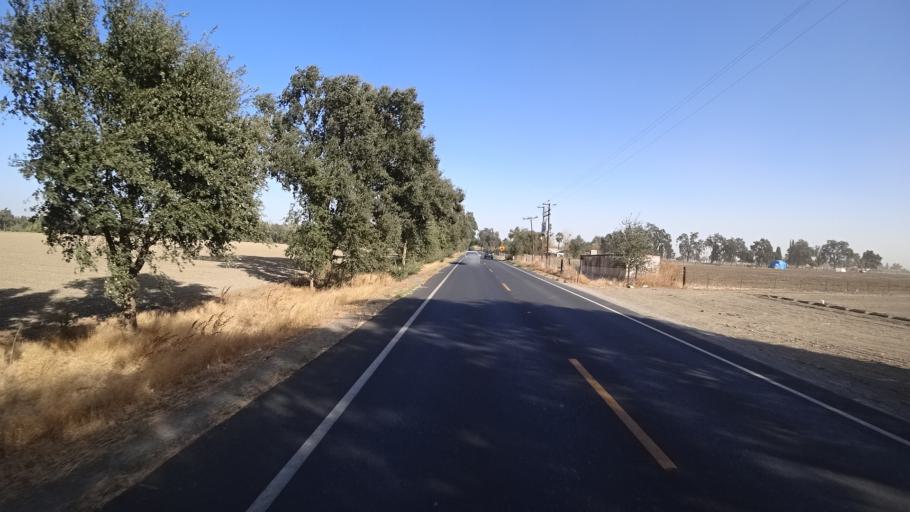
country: US
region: California
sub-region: Yolo County
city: Woodland
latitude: 38.7926
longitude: -121.7316
